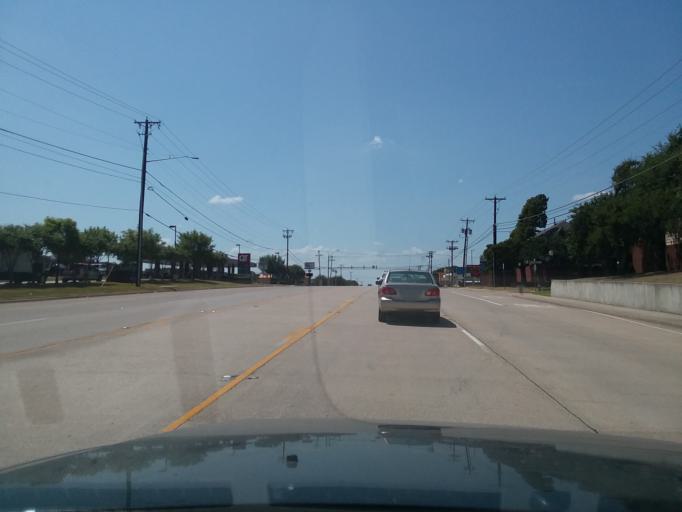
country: US
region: Texas
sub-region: Tarrant County
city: Euless
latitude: 32.8537
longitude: -97.1000
